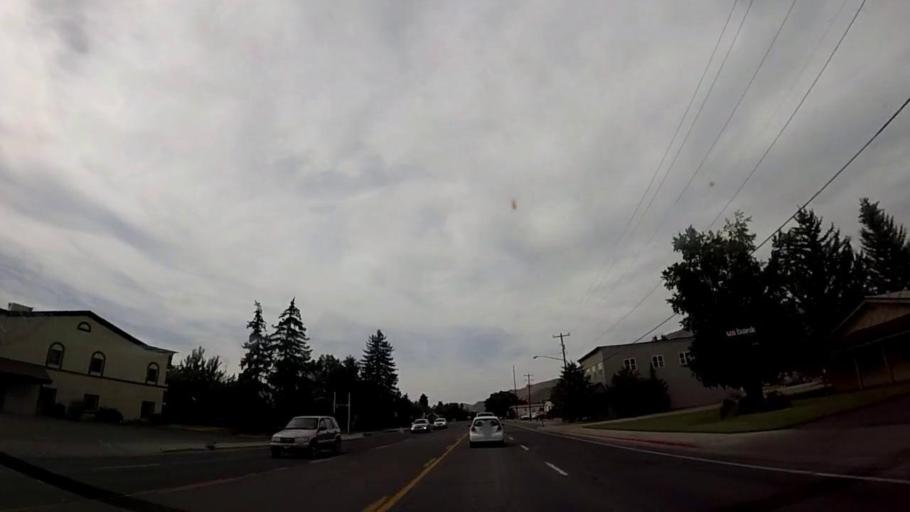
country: US
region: Idaho
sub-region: Blaine County
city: Bellevue
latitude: 43.4585
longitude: -114.2581
